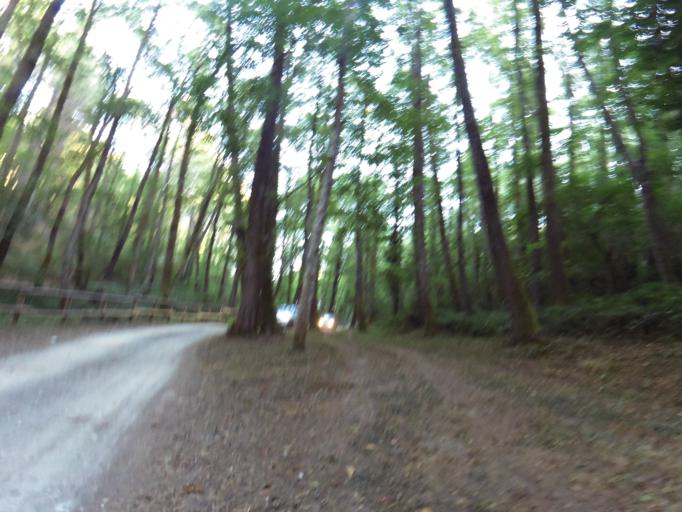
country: IT
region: Calabria
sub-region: Provincia di Vibo-Valentia
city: Mongiana
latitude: 38.5174
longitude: 16.3127
